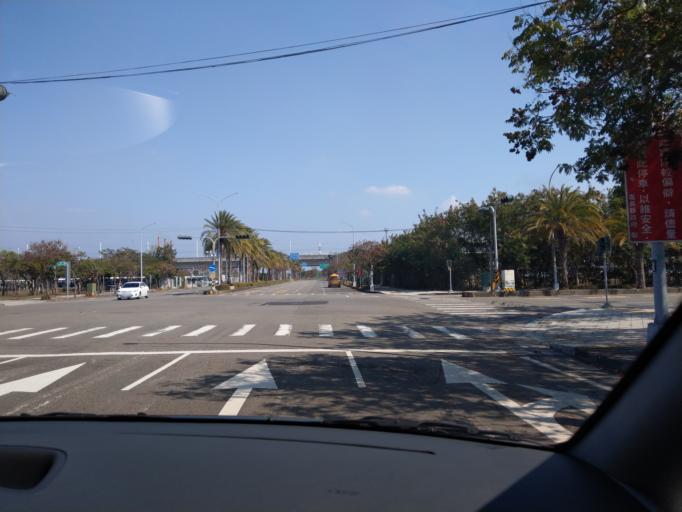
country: TW
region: Taiwan
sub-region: Chiayi
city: Taibao
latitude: 23.4613
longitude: 120.3208
